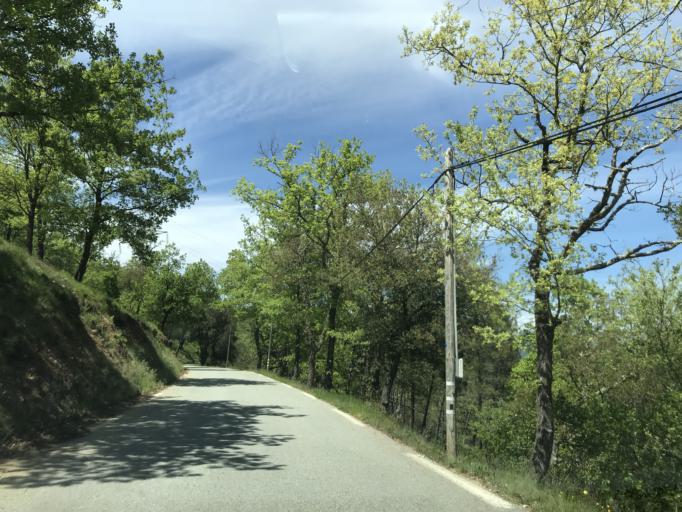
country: FR
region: Provence-Alpes-Cote d'Azur
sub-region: Departement du Var
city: Tanneron
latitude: 43.5818
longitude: 6.8242
